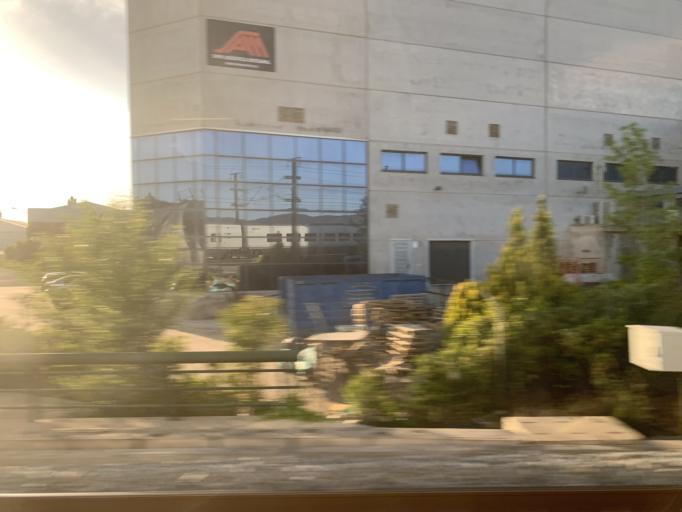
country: ES
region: Catalonia
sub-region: Provincia de Barcelona
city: Montornes del Valles
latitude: 41.5582
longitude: 2.2768
